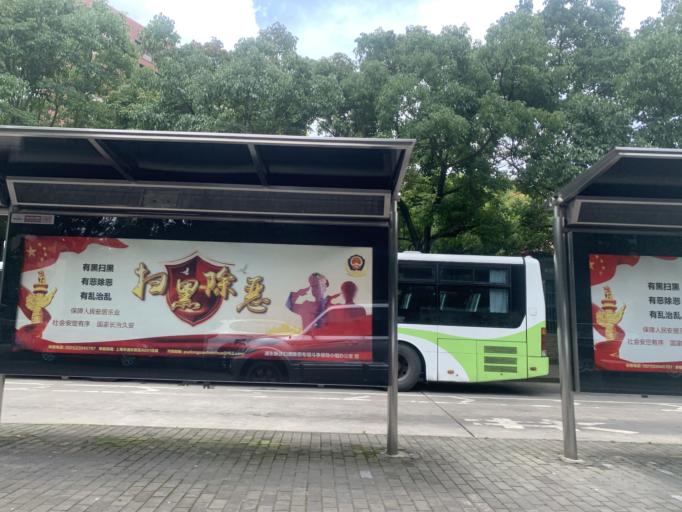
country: CN
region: Shanghai Shi
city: Huamu
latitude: 31.2038
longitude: 121.5322
